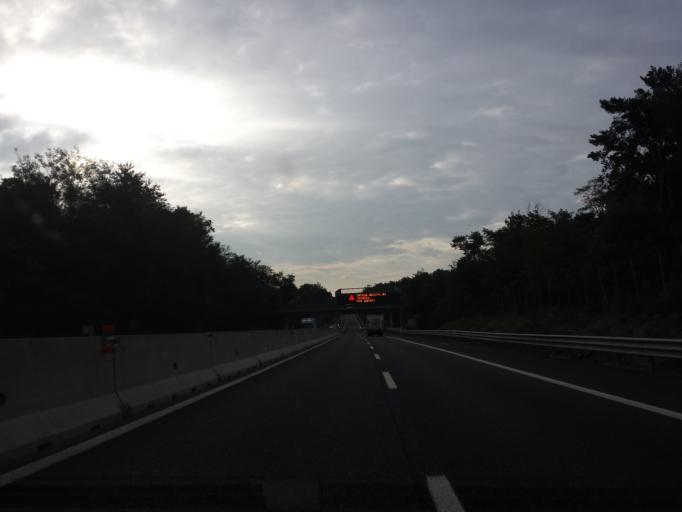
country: IT
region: Lombardy
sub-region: Provincia di Varese
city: Vergiate
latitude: 45.7141
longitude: 8.7111
